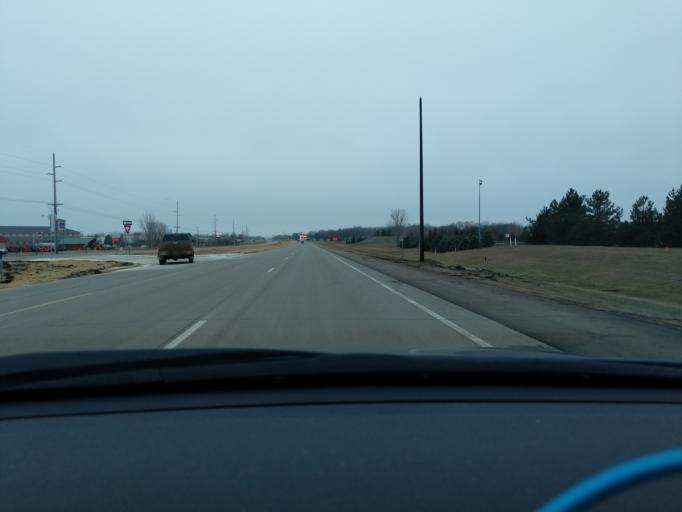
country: US
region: Minnesota
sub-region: Lyon County
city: Marshall
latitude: 44.4412
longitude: -95.7658
